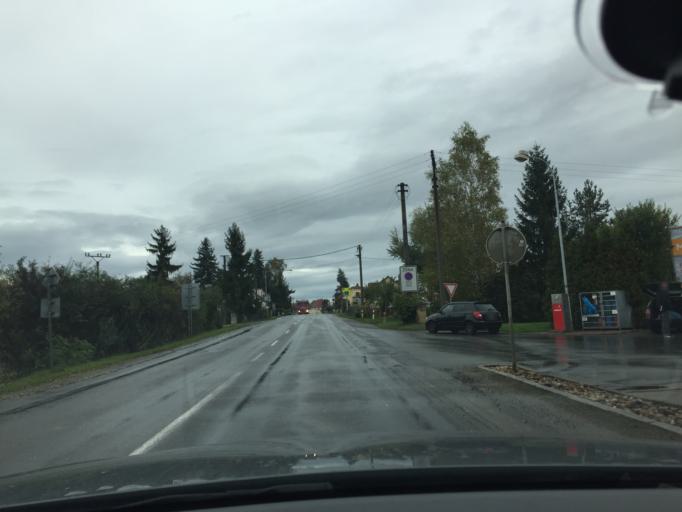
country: CZ
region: Central Bohemia
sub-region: Okres Melnik
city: Veltrusy
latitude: 50.3096
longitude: 14.3127
